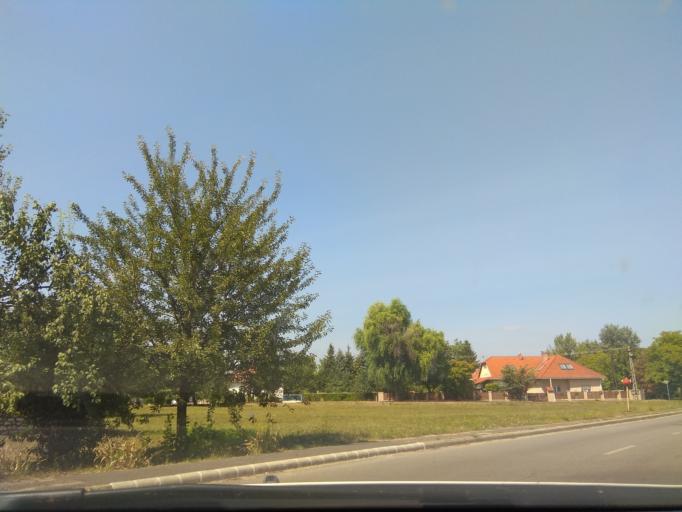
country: HU
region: Borsod-Abauj-Zemplen
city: Miskolc
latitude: 48.0633
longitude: 20.7832
